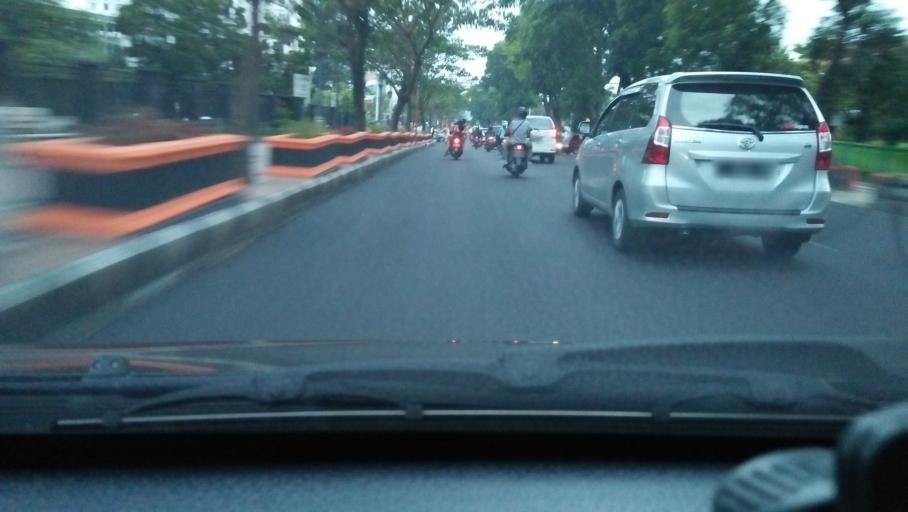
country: ID
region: Central Java
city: Mertoyudan
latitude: -7.4981
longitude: 110.2234
